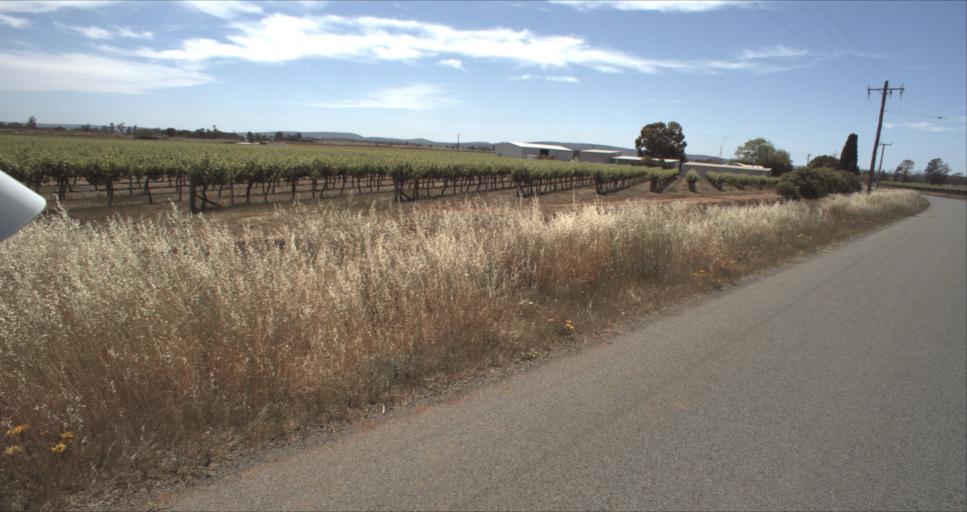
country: AU
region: New South Wales
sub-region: Leeton
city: Leeton
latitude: -34.5703
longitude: 146.4397
